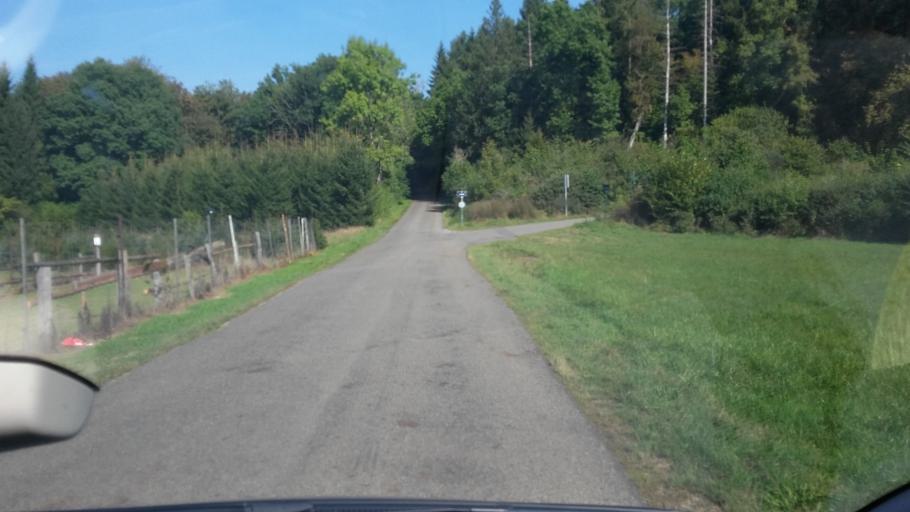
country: BE
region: Wallonia
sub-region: Province du Luxembourg
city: Arlon
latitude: 49.7107
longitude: 5.8383
